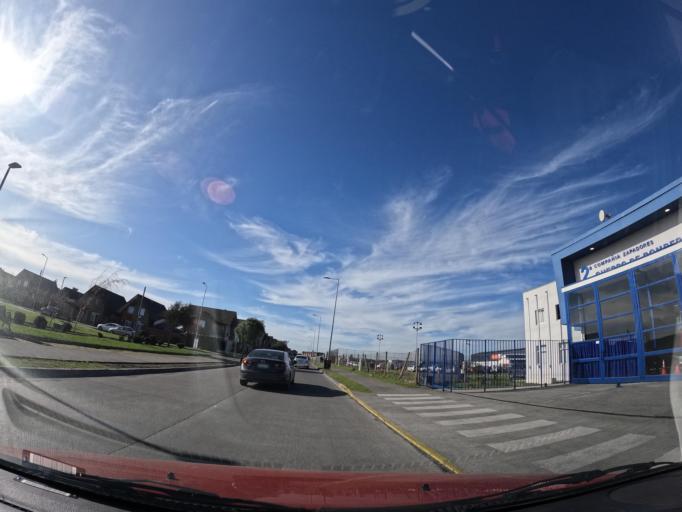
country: CL
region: Biobio
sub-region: Provincia de Concepcion
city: Concepcion
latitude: -36.7715
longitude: -73.0663
